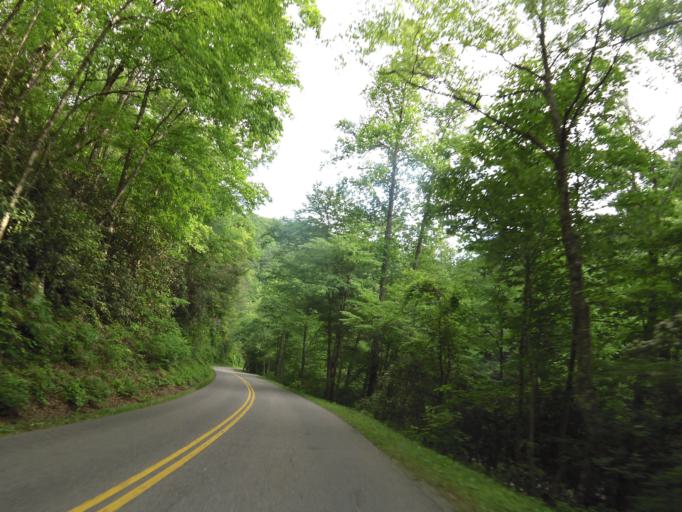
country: US
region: Tennessee
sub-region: Sevier County
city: Gatlinburg
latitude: 35.6688
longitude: -83.6284
